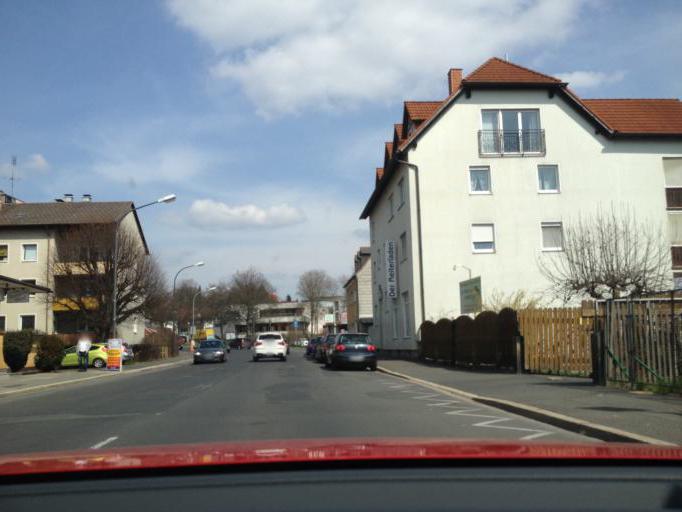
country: DE
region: Bavaria
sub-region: Upper Franconia
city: Marktredwitz
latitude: 50.0031
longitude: 12.0941
